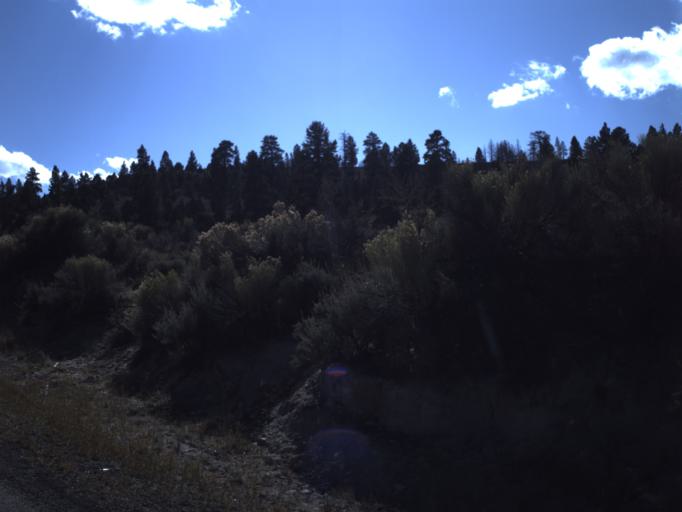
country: US
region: Utah
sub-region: Garfield County
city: Panguitch
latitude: 37.7412
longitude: -112.5905
